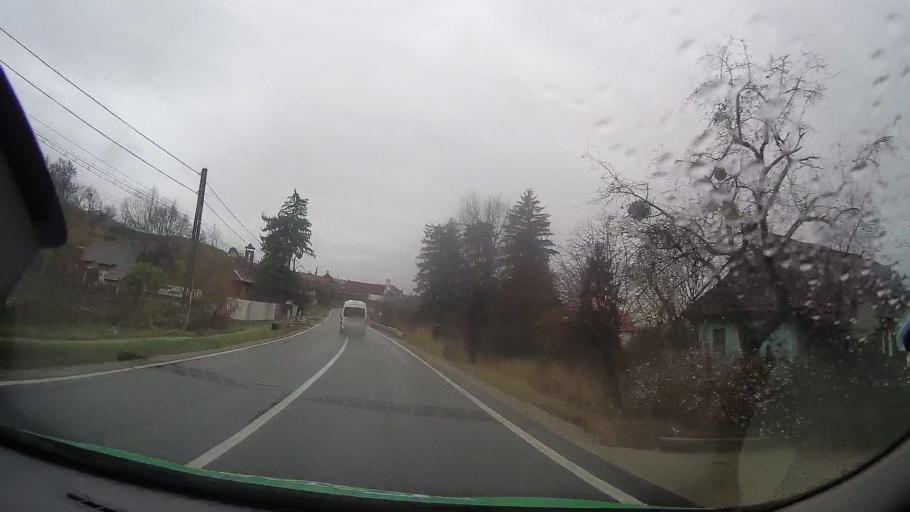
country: RO
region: Bistrita-Nasaud
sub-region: Comuna Galatii Bistritei
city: Galatii Bistritei
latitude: 47.0218
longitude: 24.4152
